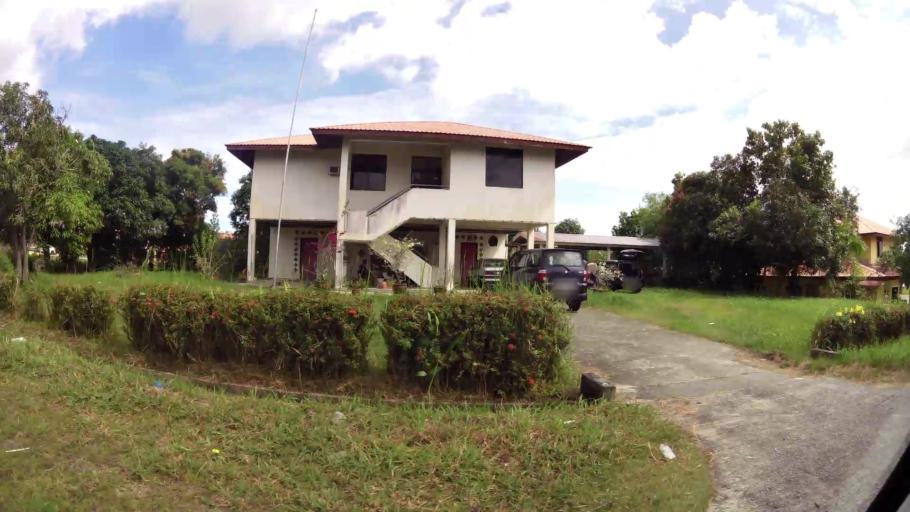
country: BN
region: Brunei and Muara
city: Bandar Seri Begawan
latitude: 4.9384
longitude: 114.9012
